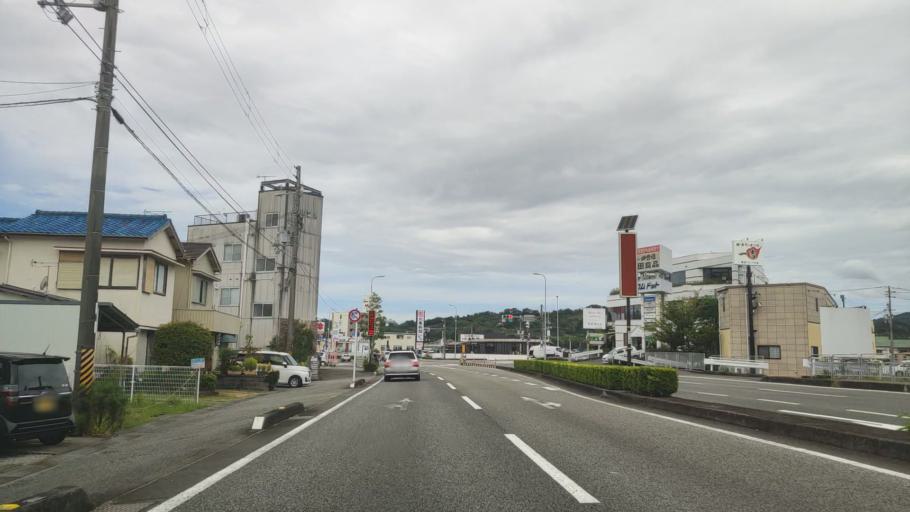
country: JP
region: Wakayama
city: Tanabe
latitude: 33.7396
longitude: 135.3936
